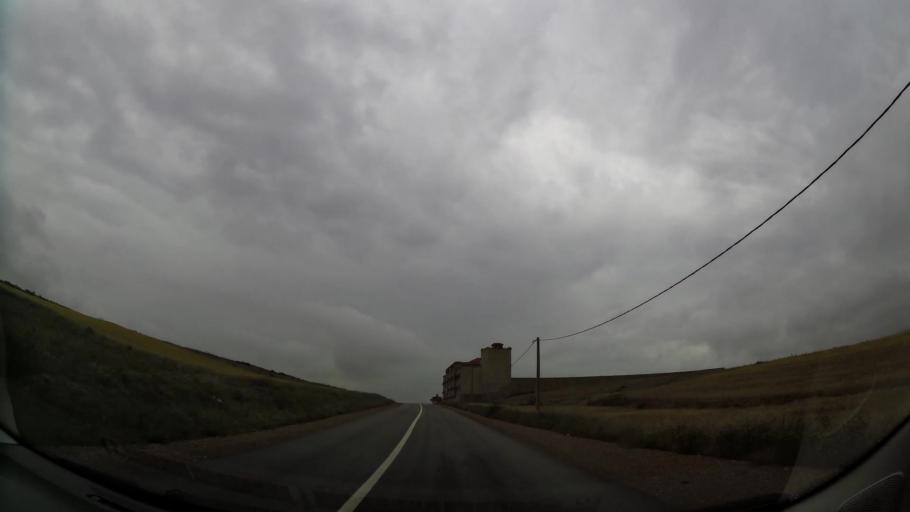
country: MA
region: Oriental
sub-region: Nador
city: Nador
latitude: 35.1523
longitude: -3.0340
